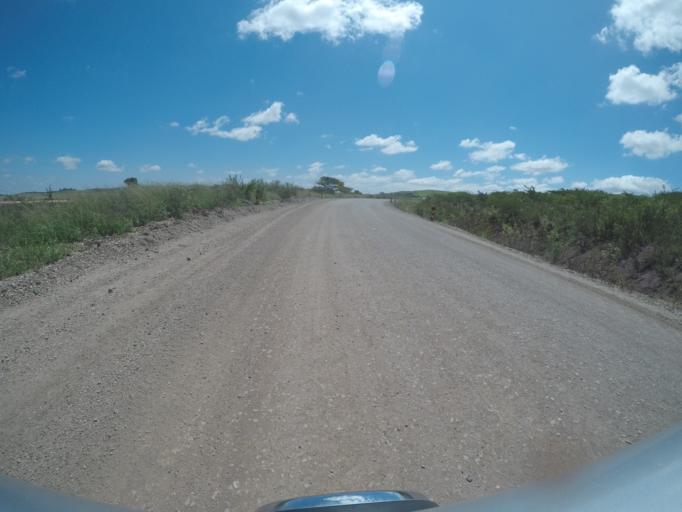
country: ZA
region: KwaZulu-Natal
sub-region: uThungulu District Municipality
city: Empangeni
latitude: -28.6616
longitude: 31.7832
